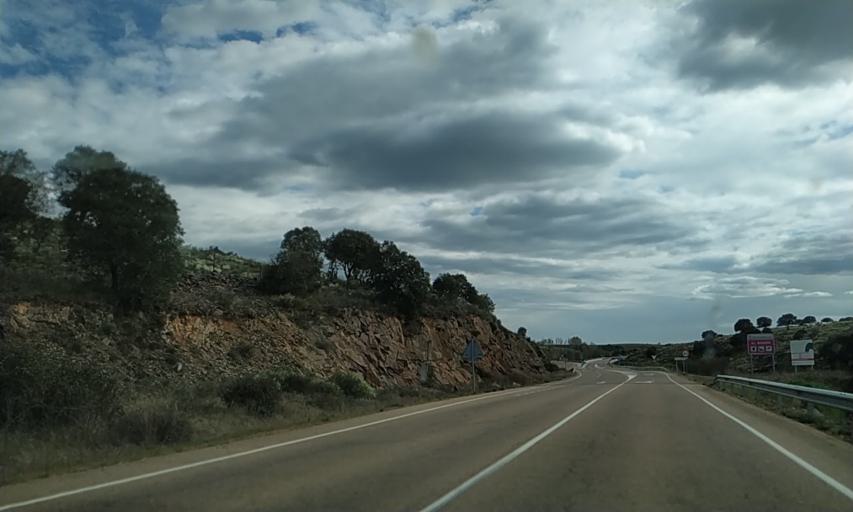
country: ES
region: Castille and Leon
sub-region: Provincia de Salamanca
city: Herguijuela de Ciudad Rodrigo
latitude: 40.4959
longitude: -6.5793
